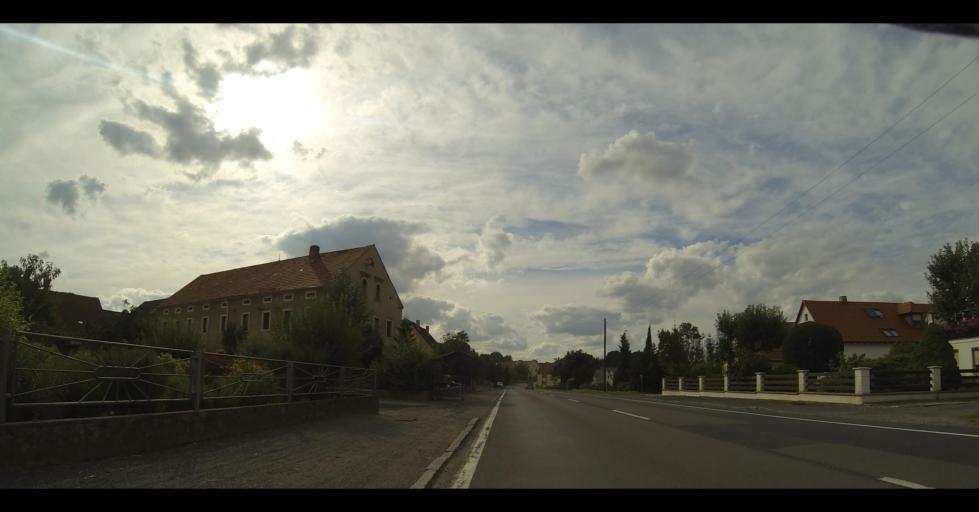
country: DE
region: Saxony
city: Radeburg
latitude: 51.2253
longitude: 13.7065
